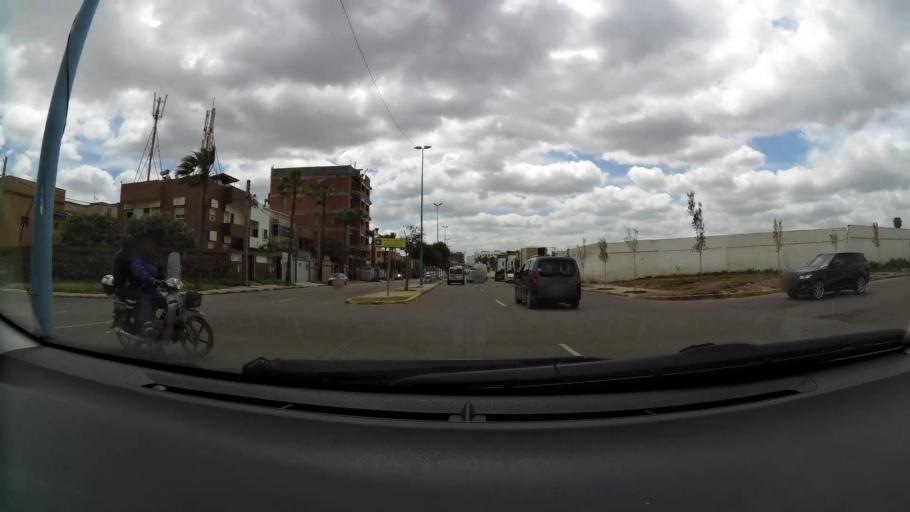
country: MA
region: Grand Casablanca
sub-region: Casablanca
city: Casablanca
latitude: 33.6097
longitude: -7.5490
